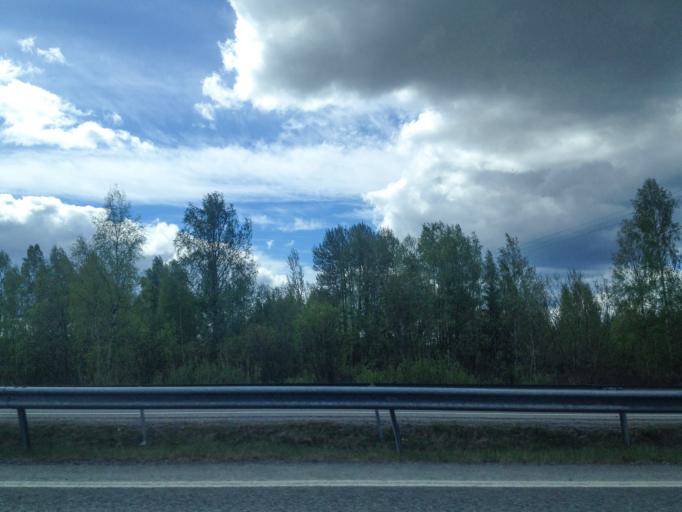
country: FI
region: Pirkanmaa
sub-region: Etelae-Pirkanmaa
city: Toijala
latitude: 61.2029
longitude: 23.8421
